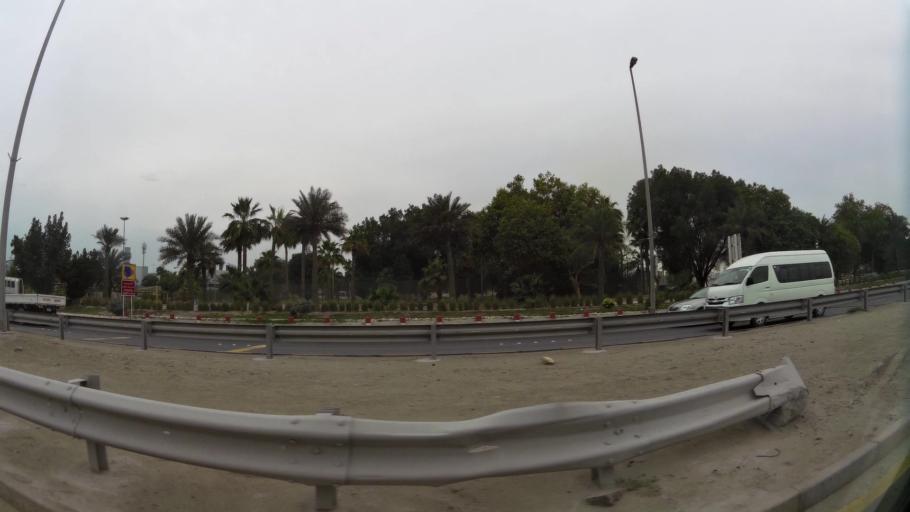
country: BH
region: Northern
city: Sitrah
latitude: 26.0973
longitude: 50.6070
